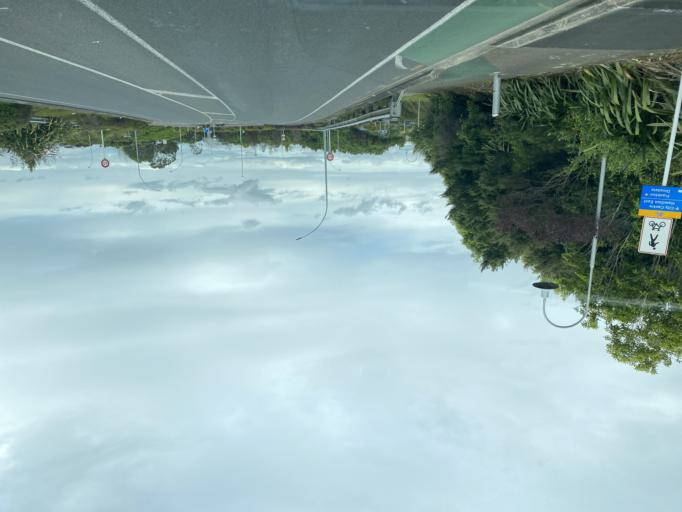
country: NZ
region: Waikato
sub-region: Hamilton City
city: Hamilton
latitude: -37.7819
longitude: 175.2514
